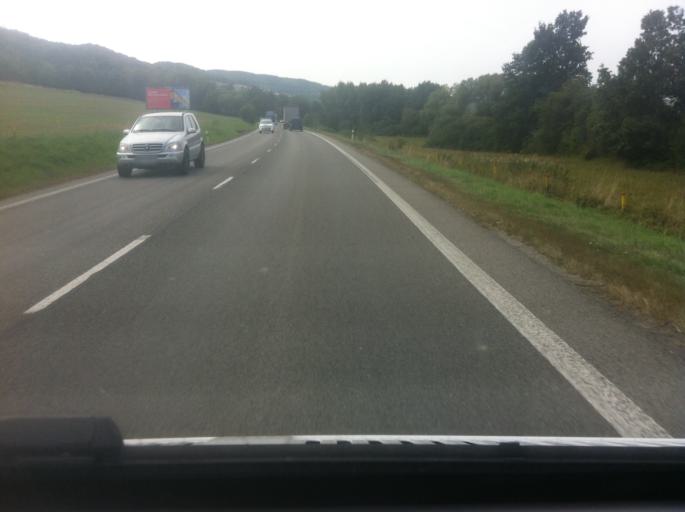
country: CZ
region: Zlin
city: Hvozdna
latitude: 49.2212
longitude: 17.7284
